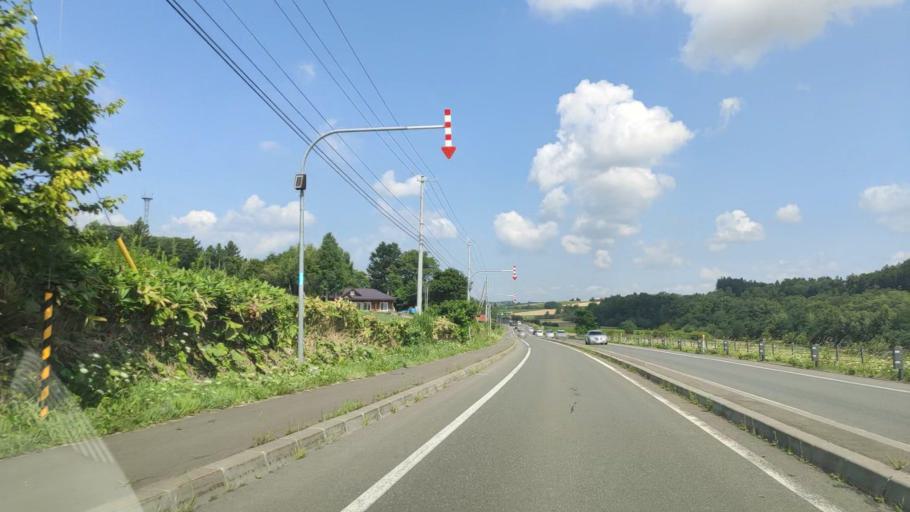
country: JP
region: Hokkaido
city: Shimo-furano
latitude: 43.5268
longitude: 142.4458
